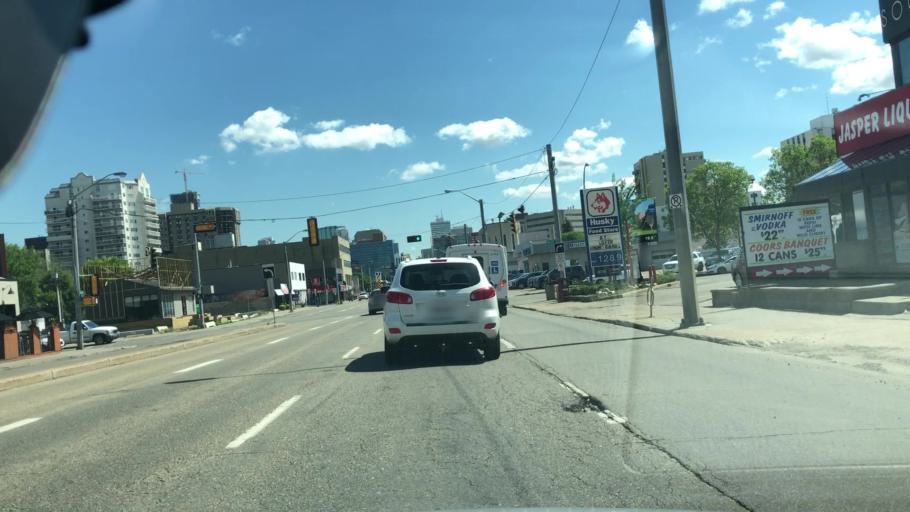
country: CA
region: Alberta
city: Edmonton
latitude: 53.5409
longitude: -113.5222
